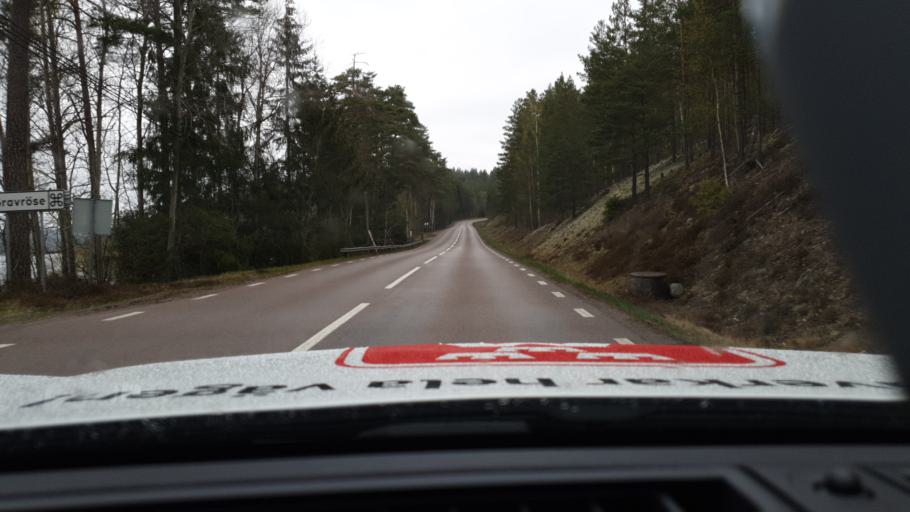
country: SE
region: Soedermanland
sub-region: Strangnas Kommun
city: Mariefred
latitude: 59.1710
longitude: 17.1852
